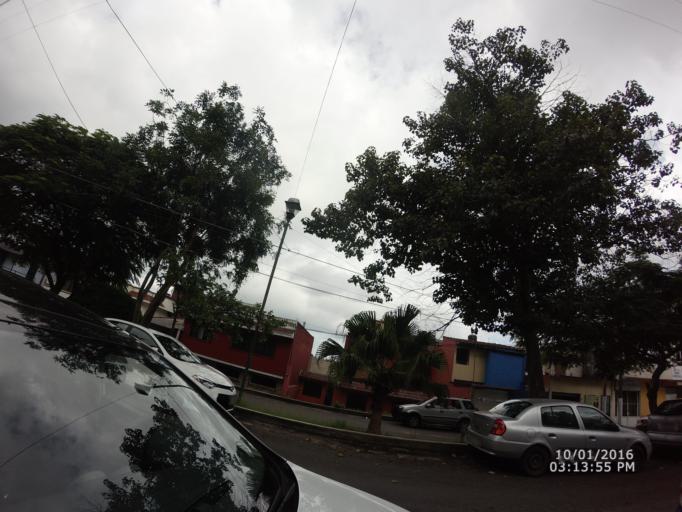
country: MX
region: Veracruz
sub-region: Xalapa
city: Xalapa de Enriquez
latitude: 19.5516
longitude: -96.9125
